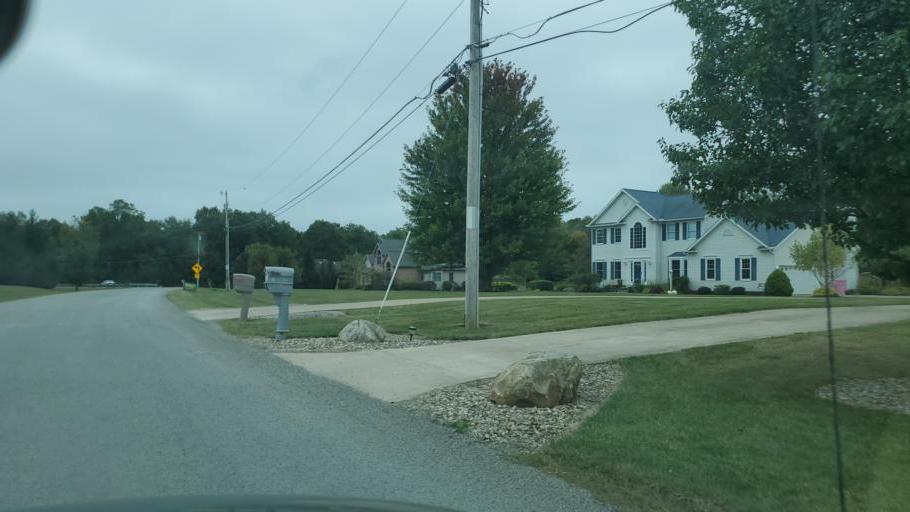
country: US
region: Ohio
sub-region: Richland County
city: Lexington
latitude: 40.6598
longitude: -82.6204
